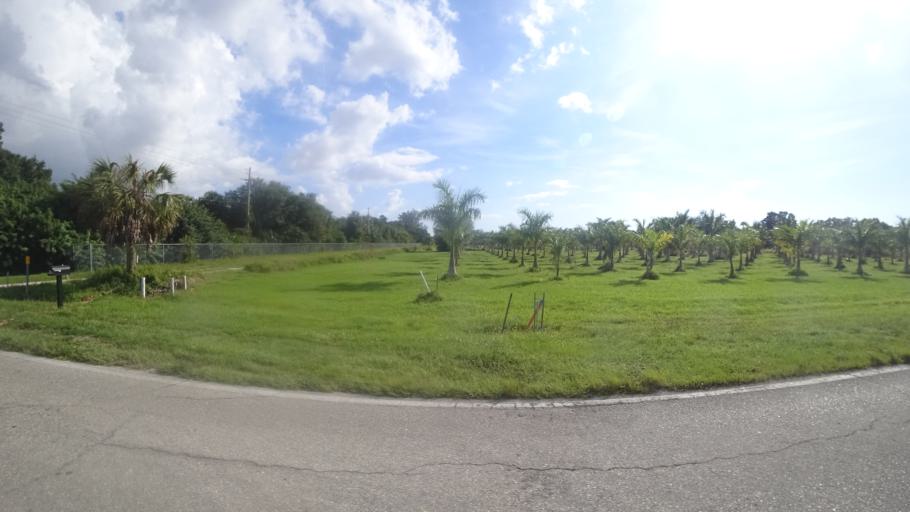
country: US
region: Florida
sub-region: Manatee County
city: West Bradenton
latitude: 27.5213
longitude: -82.5976
